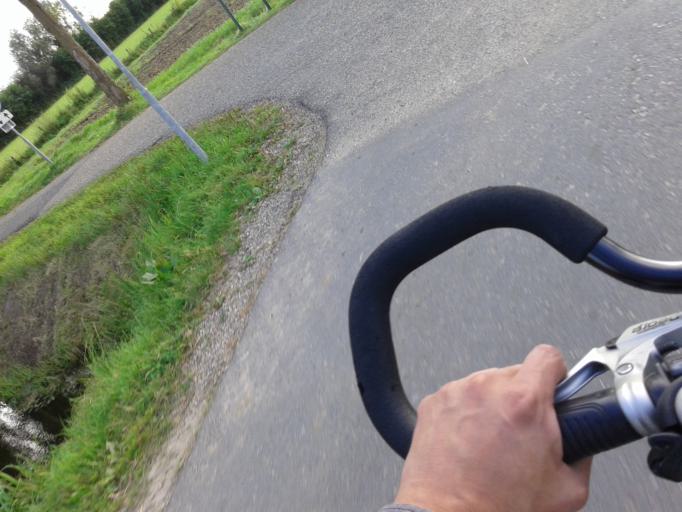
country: NL
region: Gelderland
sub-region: Gemeente Wageningen
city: Wageningen
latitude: 51.9897
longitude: 5.6486
